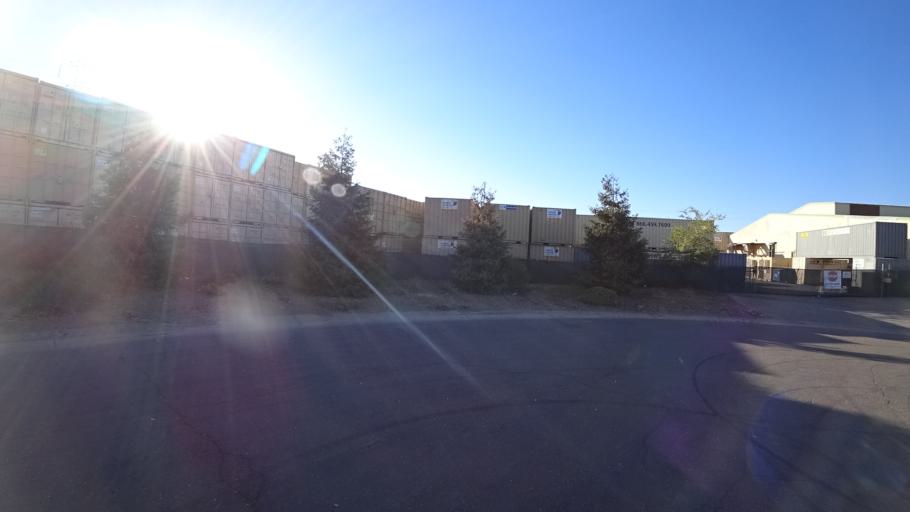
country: US
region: California
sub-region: Sacramento County
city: Florin
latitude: 38.5188
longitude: -121.3864
